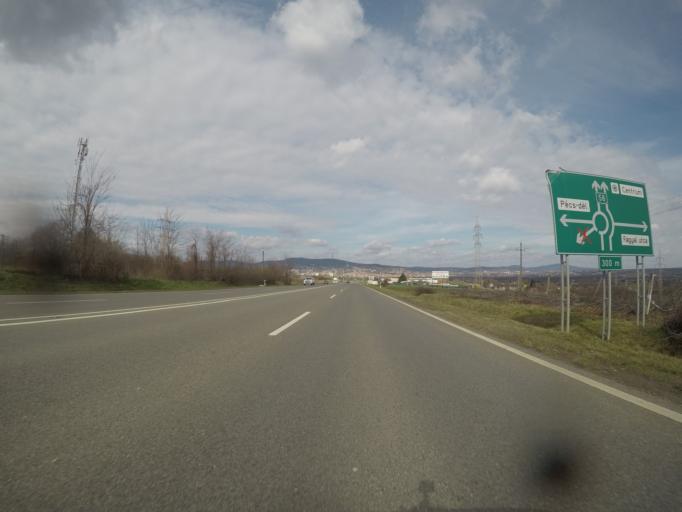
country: HU
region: Baranya
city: Pecs
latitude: 46.0325
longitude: 18.2332
